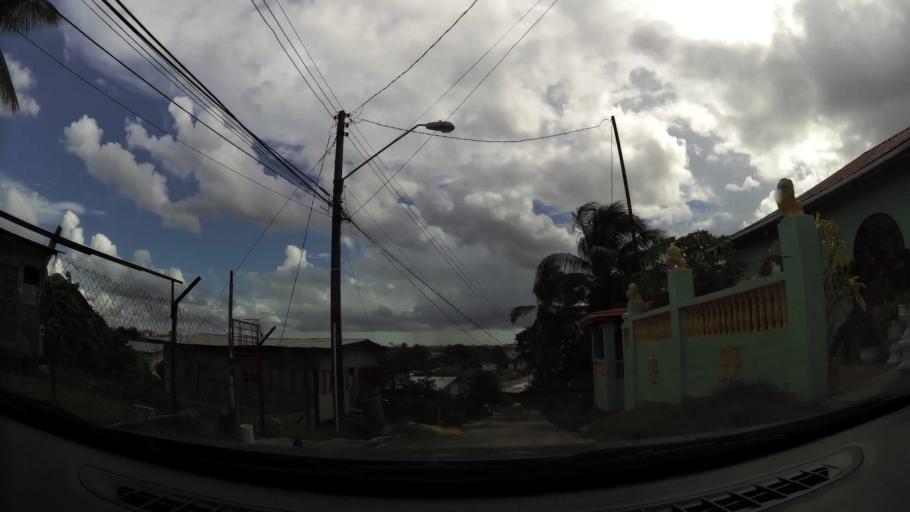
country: TT
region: City of San Fernando
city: Mon Repos
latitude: 10.2750
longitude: -61.4476
